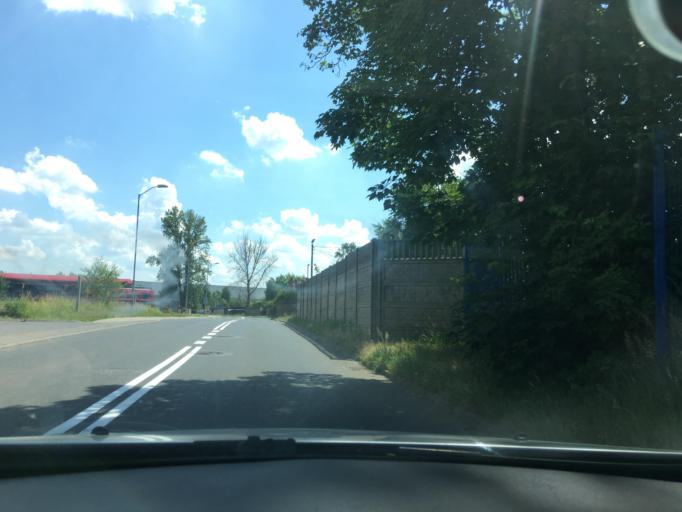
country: PL
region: Silesian Voivodeship
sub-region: Swietochlowice
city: Swietochlowice
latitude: 50.2692
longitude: 18.9475
